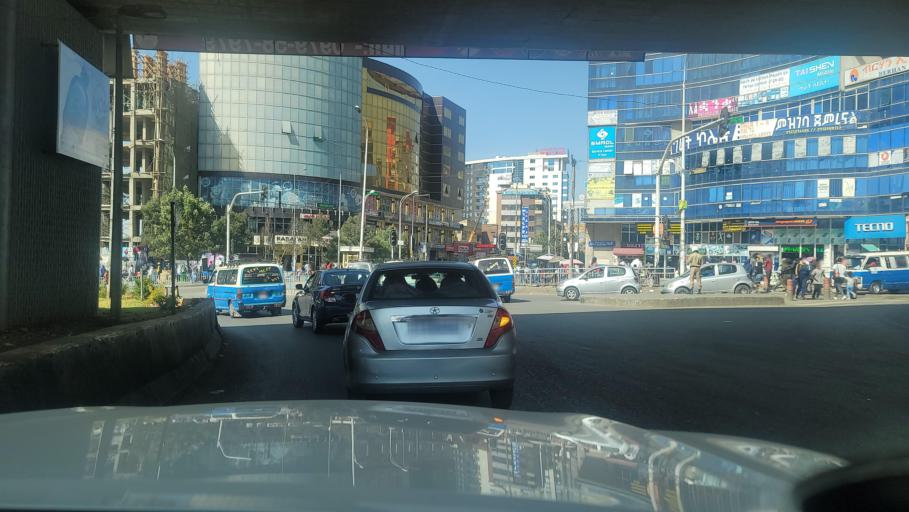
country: ET
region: Adis Abeba
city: Addis Ababa
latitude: 9.0200
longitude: 38.8015
